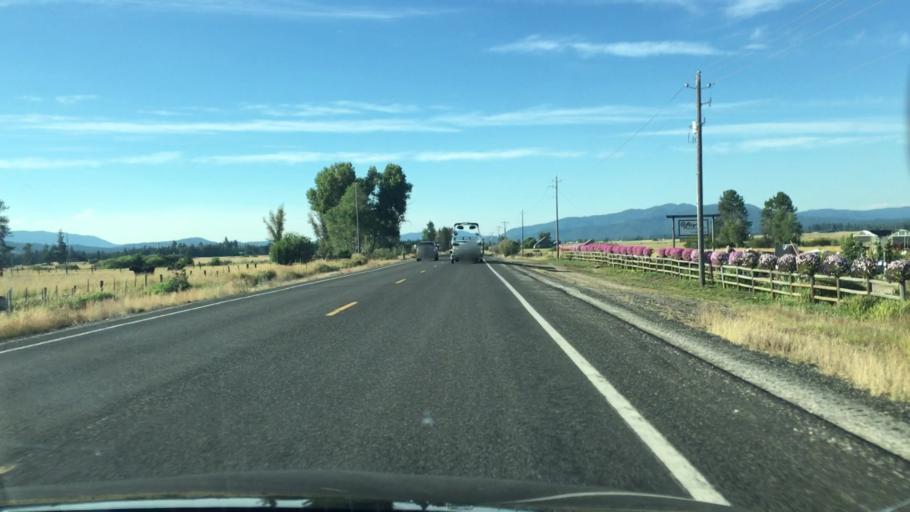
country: US
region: Idaho
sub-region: Valley County
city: Cascade
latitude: 44.4255
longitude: -115.9995
